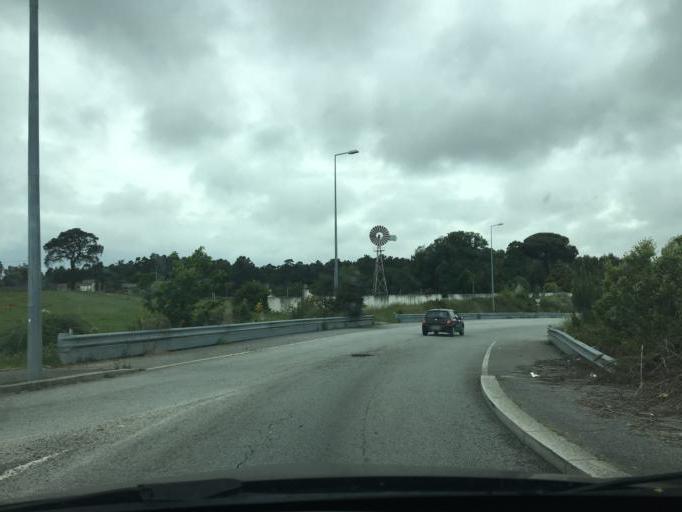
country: PT
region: Porto
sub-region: Matosinhos
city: Santa Cruz do Bispo
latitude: 41.2213
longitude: -8.6708
